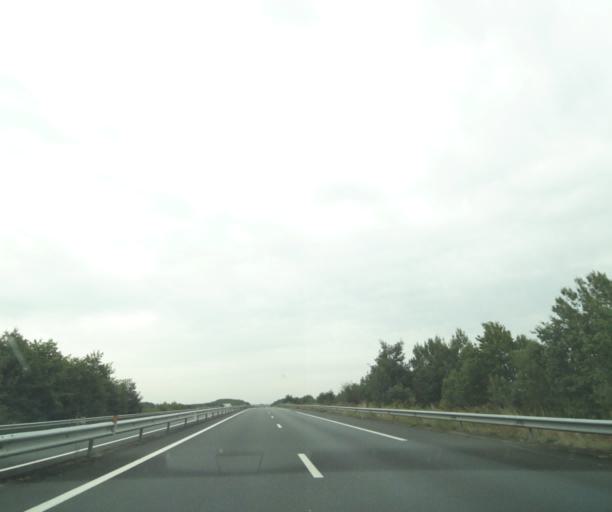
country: FR
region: Pays de la Loire
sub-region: Departement de la Vendee
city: Bouffere
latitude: 46.9377
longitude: -1.3452
